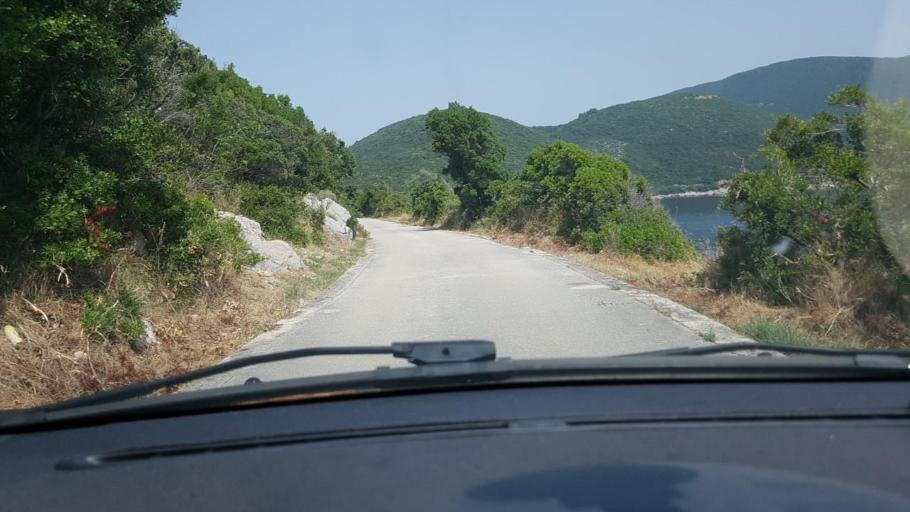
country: ME
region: Herceg Novi
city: Herceg-Novi
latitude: 42.4042
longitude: 18.5138
